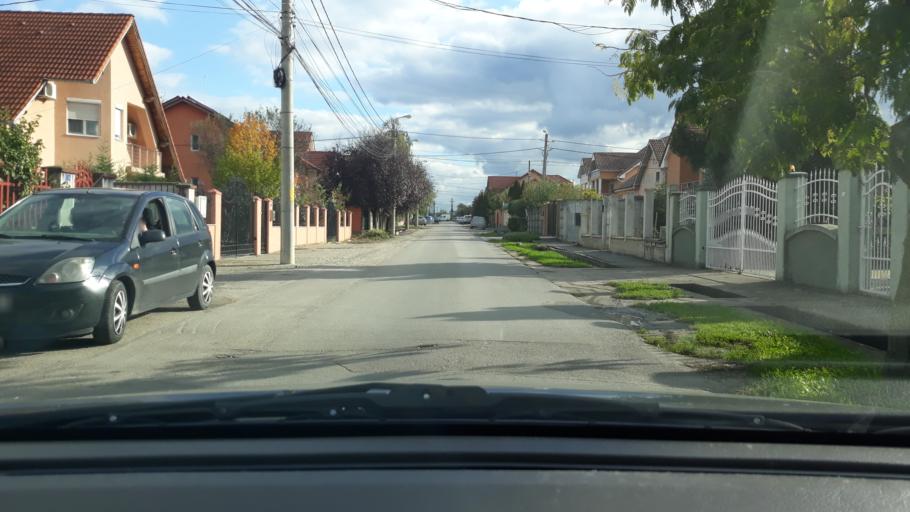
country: RO
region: Bihor
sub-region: Comuna Sanmartin
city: Sanmartin
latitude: 47.0281
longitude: 21.9471
